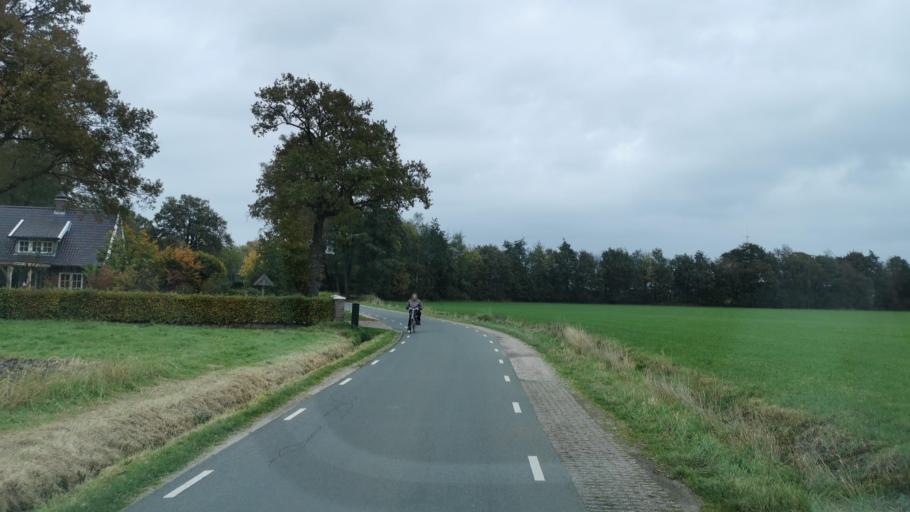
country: NL
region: Overijssel
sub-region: Gemeente Losser
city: Losser
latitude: 52.2502
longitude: 6.9991
